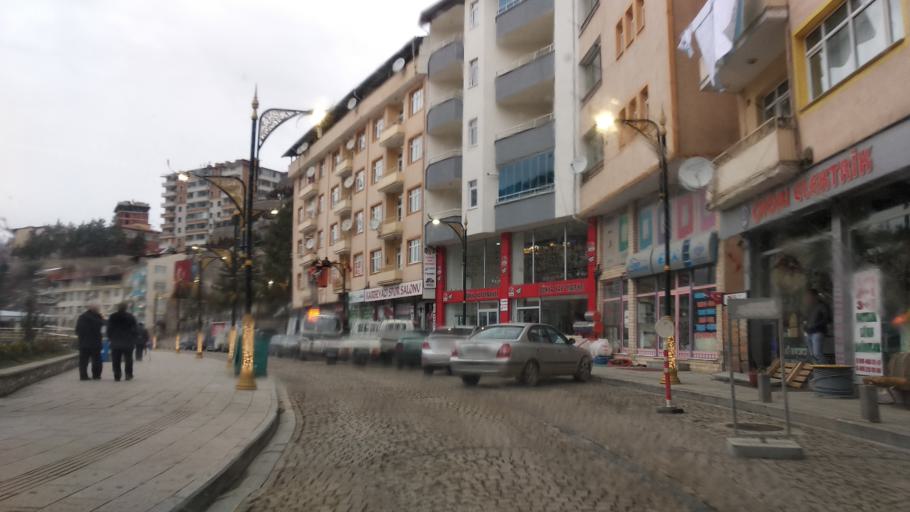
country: TR
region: Gumushane
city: Gumushkhane
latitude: 40.4585
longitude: 39.4859
